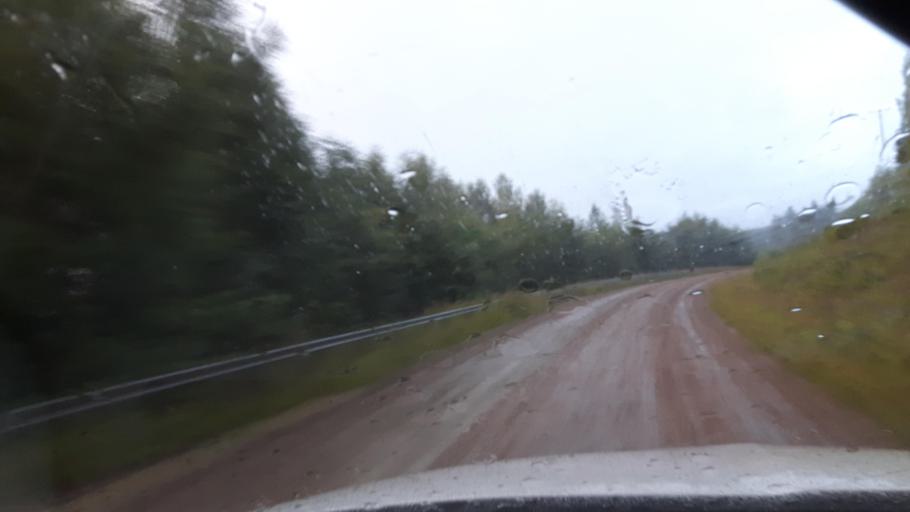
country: SE
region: Vaesternorrland
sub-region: Ange Kommun
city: Ange
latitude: 62.1540
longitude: 15.6633
